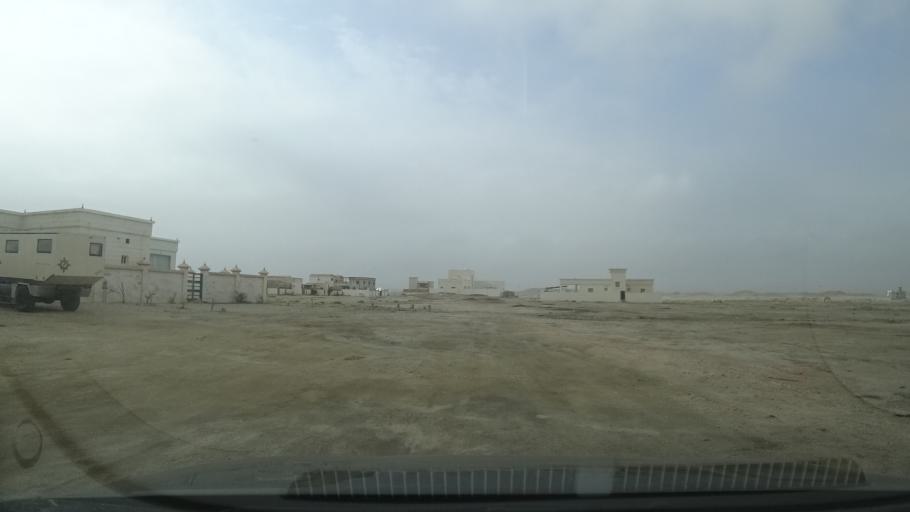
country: OM
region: Zufar
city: Salalah
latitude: 16.9674
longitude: 54.7376
